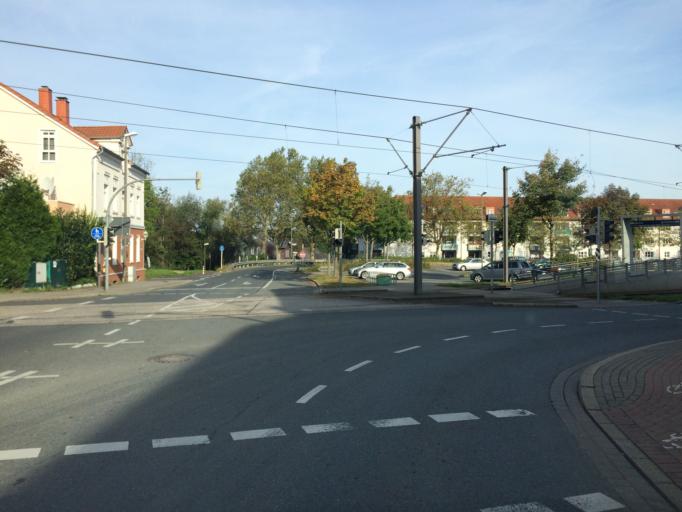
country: DE
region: North Rhine-Westphalia
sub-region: Regierungsbezirk Arnsberg
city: Dortmund
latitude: 51.4864
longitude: 7.4359
